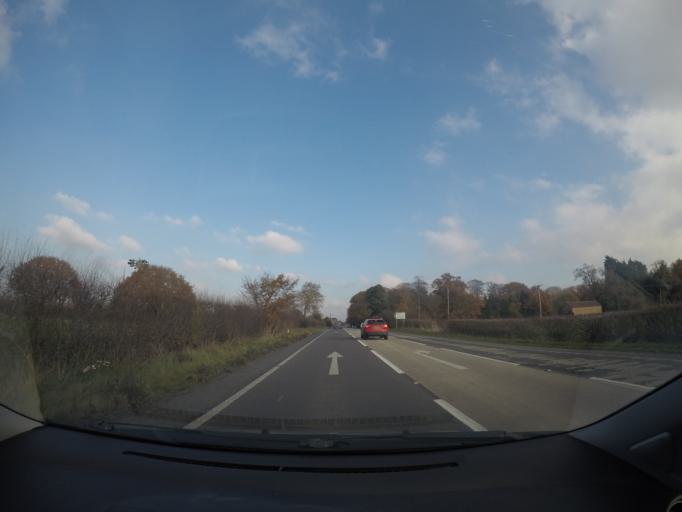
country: GB
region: England
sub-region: City of York
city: Holtby
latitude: 54.0126
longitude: -0.9911
